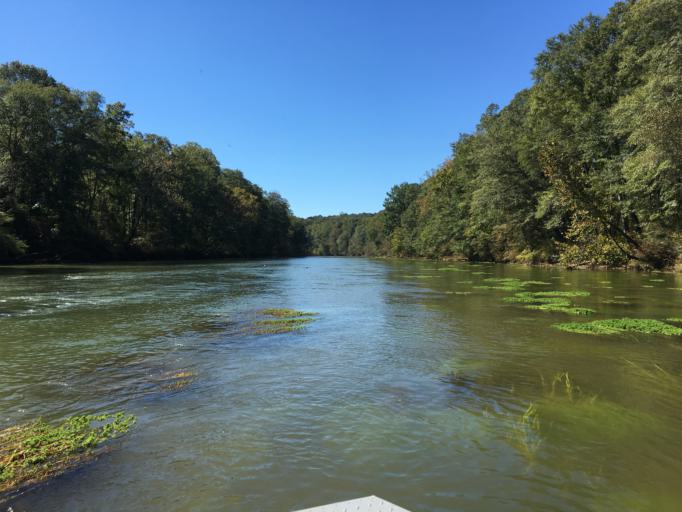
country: US
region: Georgia
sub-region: Fulton County
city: Johns Creek
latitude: 33.9997
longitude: -84.2419
